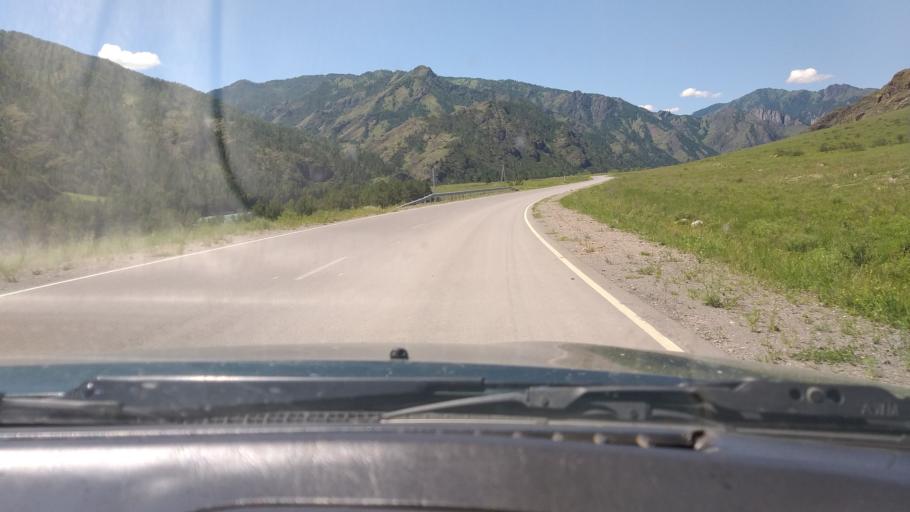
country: RU
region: Altay
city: Chemal
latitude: 51.1637
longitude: 86.1375
